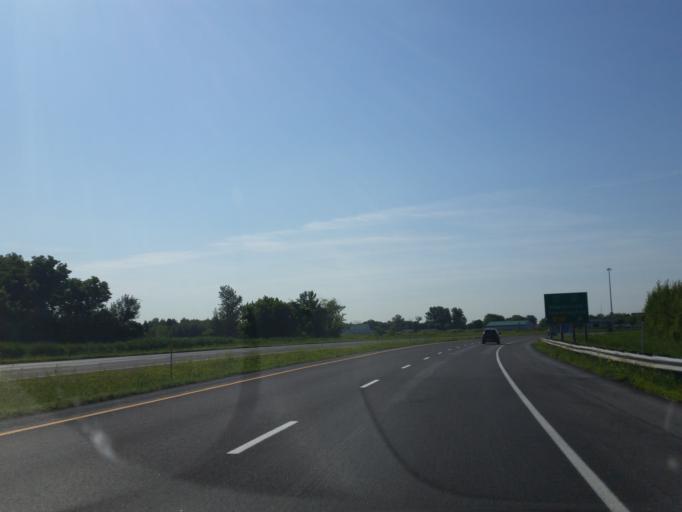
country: CA
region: Quebec
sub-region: Monteregie
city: Napierville
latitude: 45.2009
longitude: -73.4578
